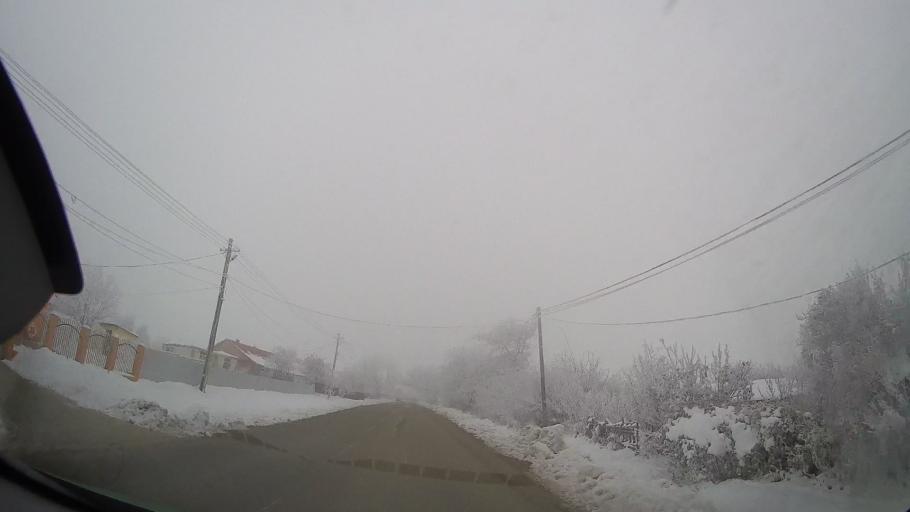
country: RO
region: Neamt
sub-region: Comuna Valea Ursului
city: Valea Ursului
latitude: 46.7966
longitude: 27.0801
